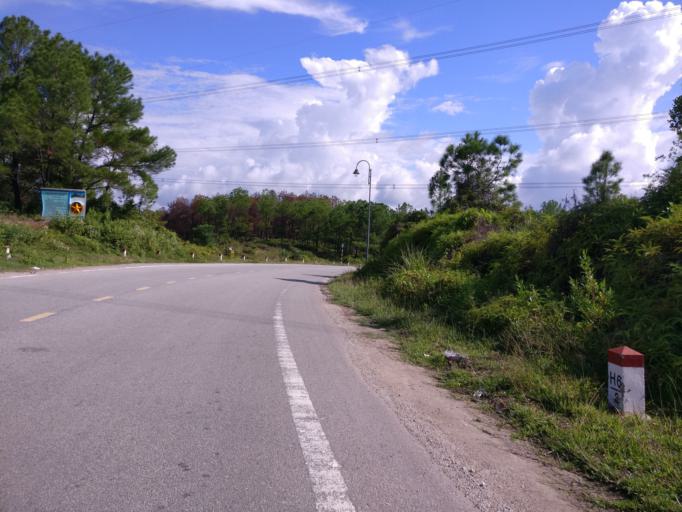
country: VN
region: Thua Thien-Hue
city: Hue
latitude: 16.4060
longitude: 107.5898
